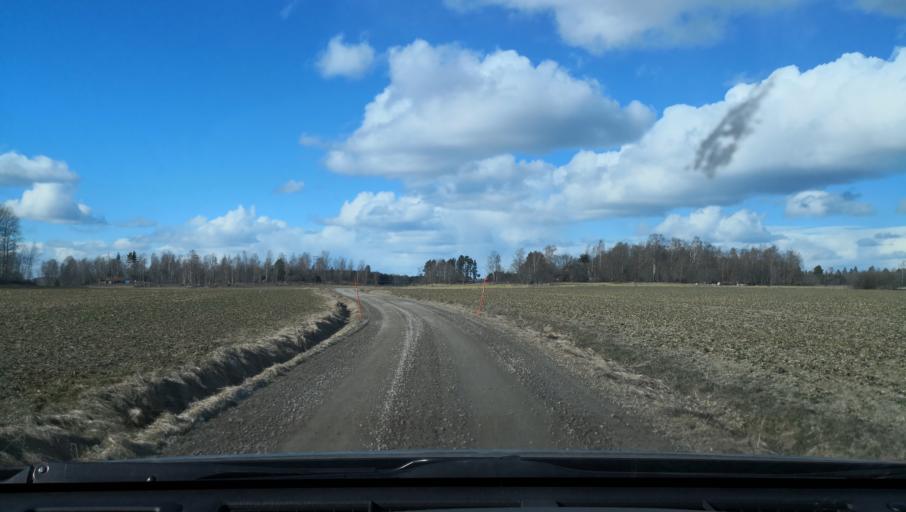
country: SE
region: OErebro
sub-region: Lindesbergs Kommun
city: Fellingsbro
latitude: 59.4205
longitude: 15.6307
